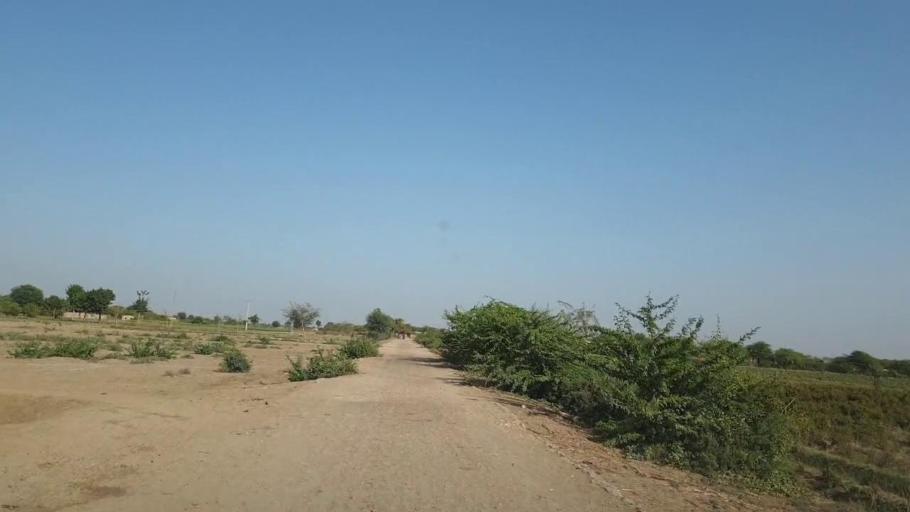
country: PK
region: Sindh
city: Naukot
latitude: 25.0314
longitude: 69.4441
